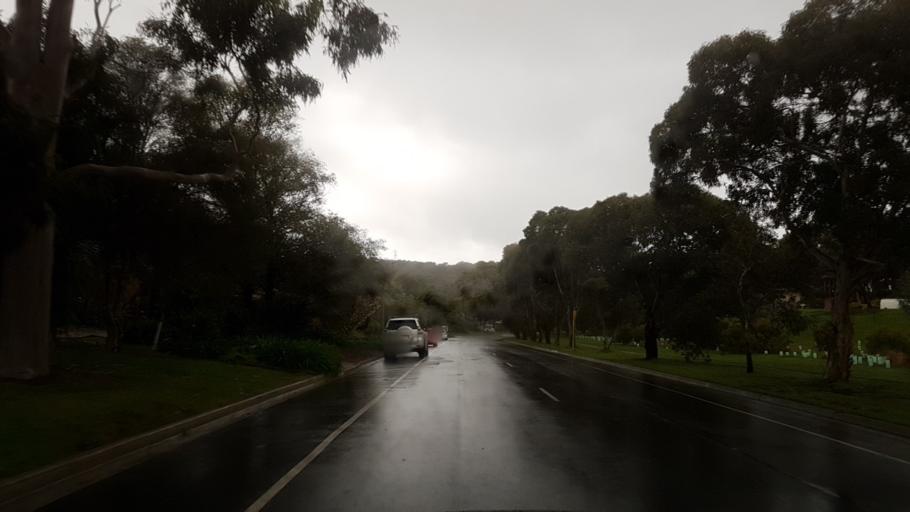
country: AU
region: South Australia
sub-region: Onkaparinga
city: Craigburn Farm
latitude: -35.0897
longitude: 138.5904
